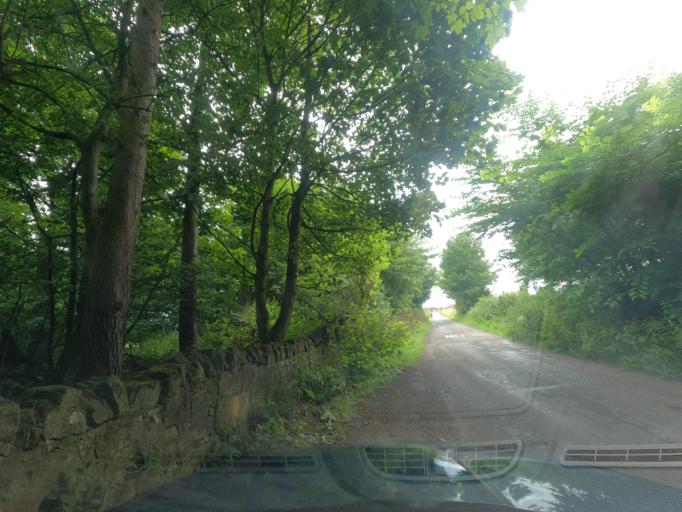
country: GB
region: England
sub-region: Northumberland
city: Ancroft
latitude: 55.7363
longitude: -1.9862
